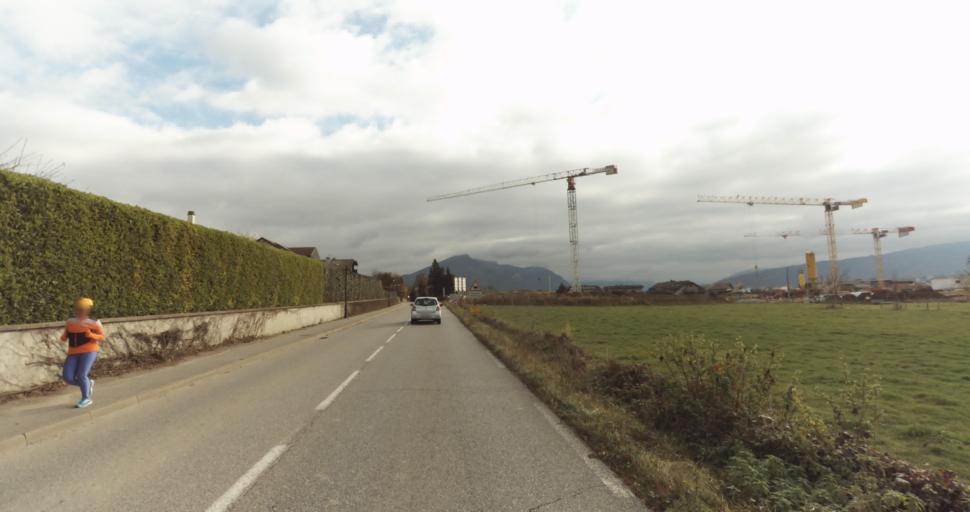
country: FR
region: Rhone-Alpes
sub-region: Departement de la Haute-Savoie
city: Epagny
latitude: 45.9386
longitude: 6.0951
